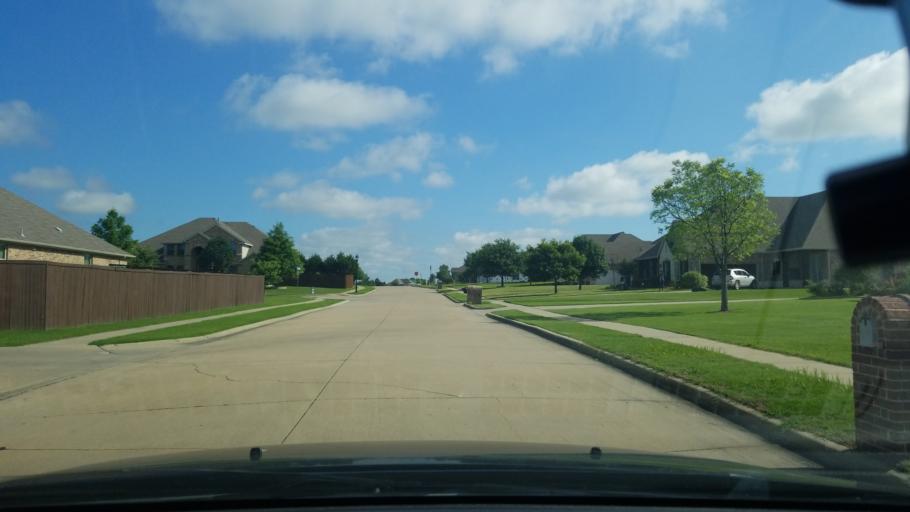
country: US
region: Texas
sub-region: Dallas County
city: Sunnyvale
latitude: 32.8055
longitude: -96.5617
